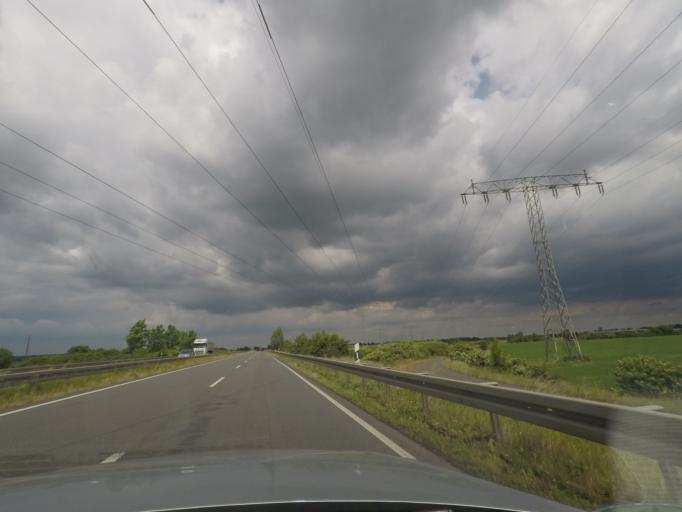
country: DE
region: Saxony
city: Markranstadt
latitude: 51.2692
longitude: 12.2662
